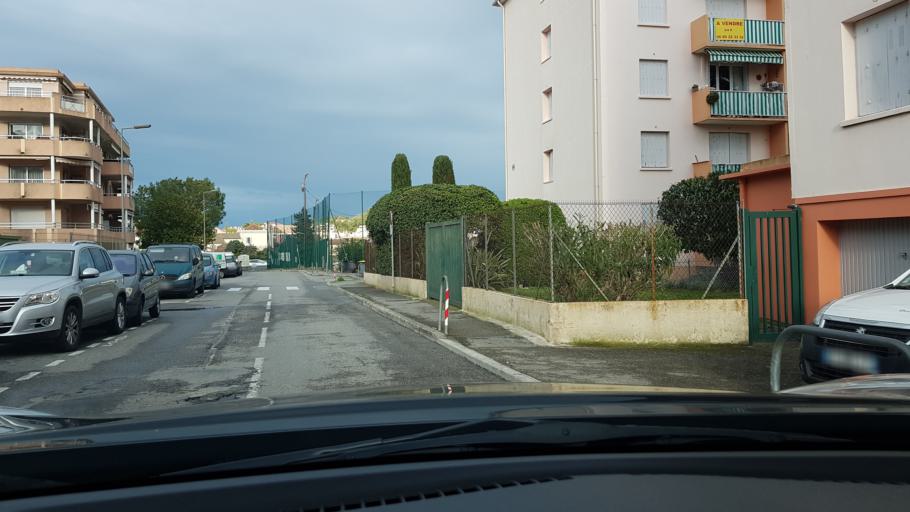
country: FR
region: Provence-Alpes-Cote d'Azur
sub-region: Departement des Alpes-Maritimes
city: Vallauris
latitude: 43.5761
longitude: 7.0511
